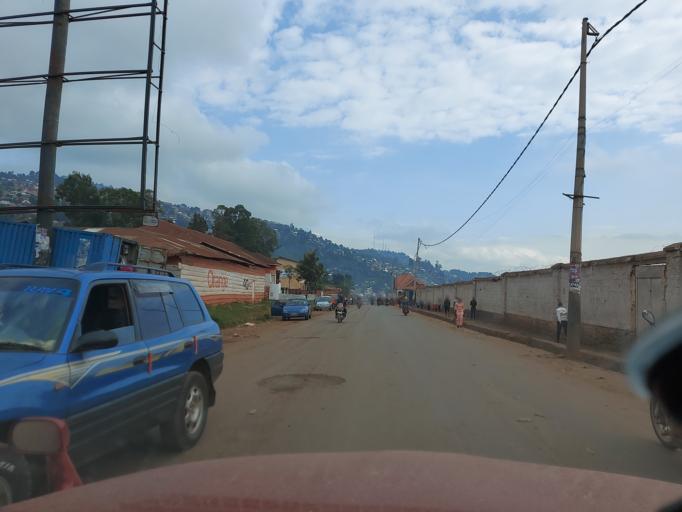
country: CD
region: South Kivu
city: Bukavu
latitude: -2.5178
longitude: 28.8513
